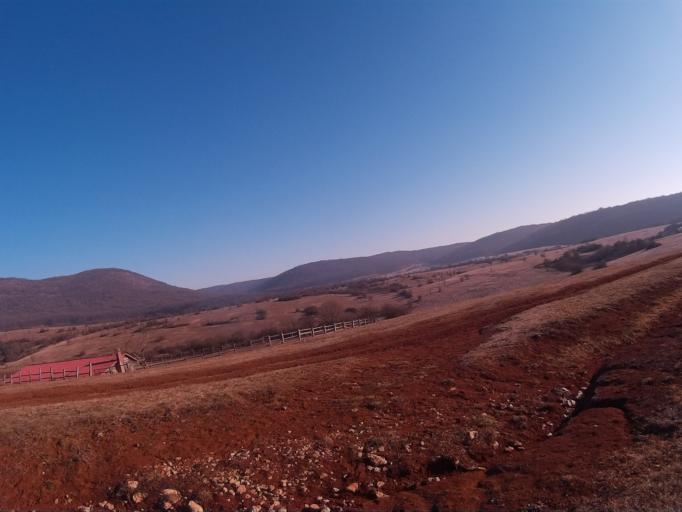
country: HU
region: Borsod-Abauj-Zemplen
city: Rudabanya
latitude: 48.4938
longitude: 20.5467
